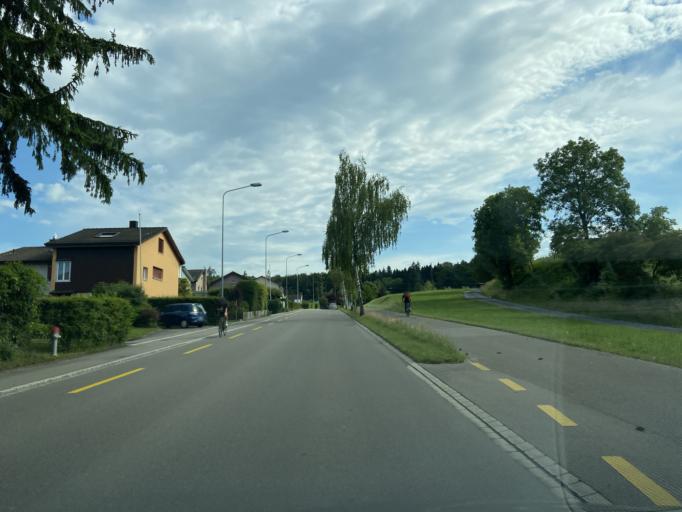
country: CH
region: Zurich
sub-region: Bezirk Winterthur
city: Seuzach Dorf
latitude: 47.5308
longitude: 8.7283
